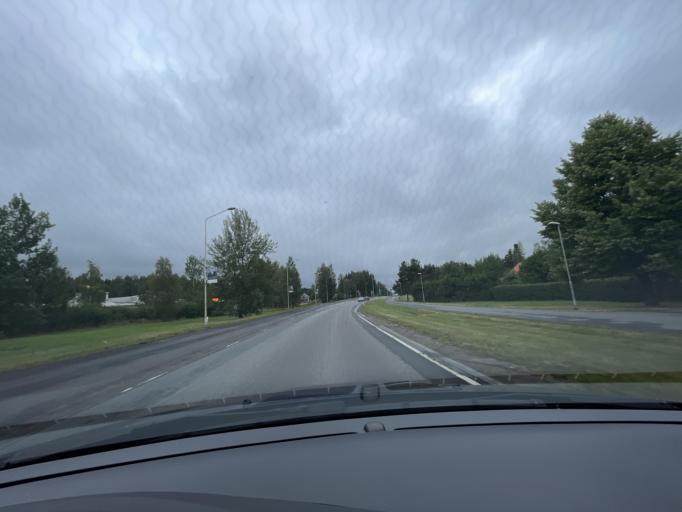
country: FI
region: Haeme
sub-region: Riihimaeki
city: Riihimaeki
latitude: 60.7257
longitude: 24.7598
